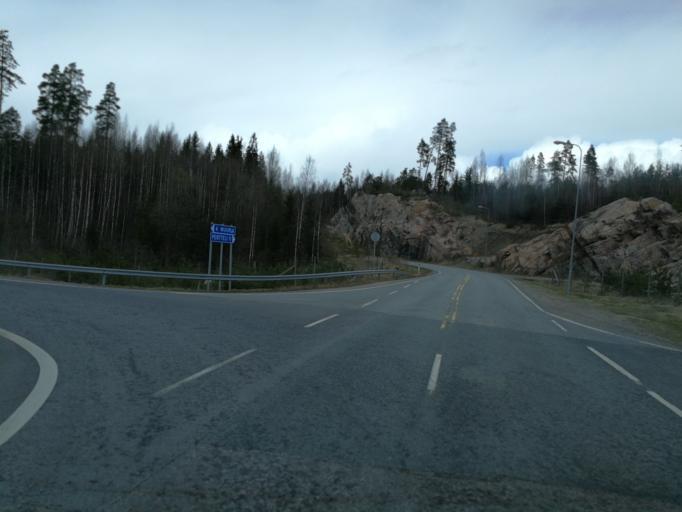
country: FI
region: Varsinais-Suomi
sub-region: Salo
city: Muurla
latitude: 60.3802
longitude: 23.3204
